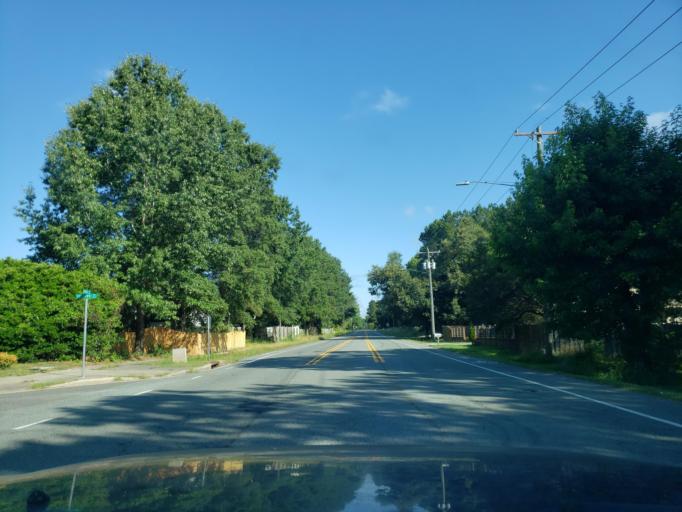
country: US
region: North Carolina
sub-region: Durham County
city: Durham
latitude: 35.9363
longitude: -78.8933
